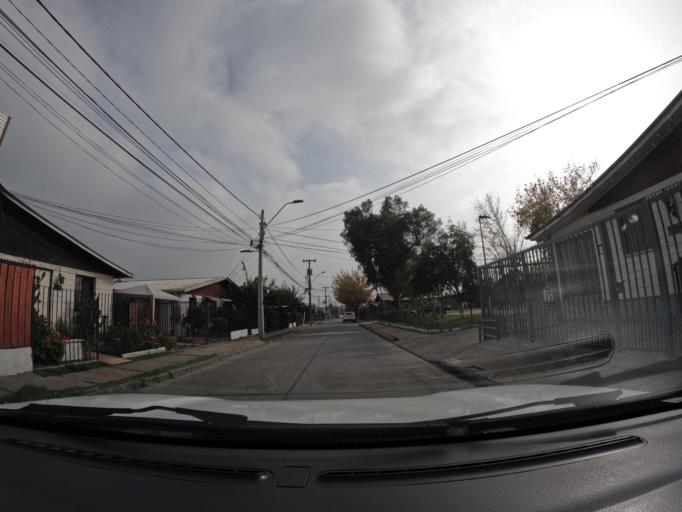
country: CL
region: Santiago Metropolitan
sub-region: Provincia de Santiago
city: Villa Presidente Frei, Nunoa, Santiago, Chile
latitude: -33.4733
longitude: -70.5503
